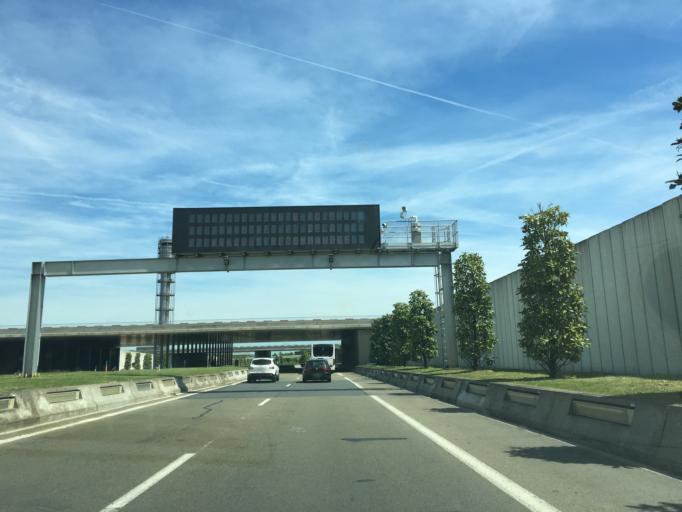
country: FR
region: Ile-de-France
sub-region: Departement de Seine-et-Marne
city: Mitry-Mory
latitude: 49.0050
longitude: 2.5931
